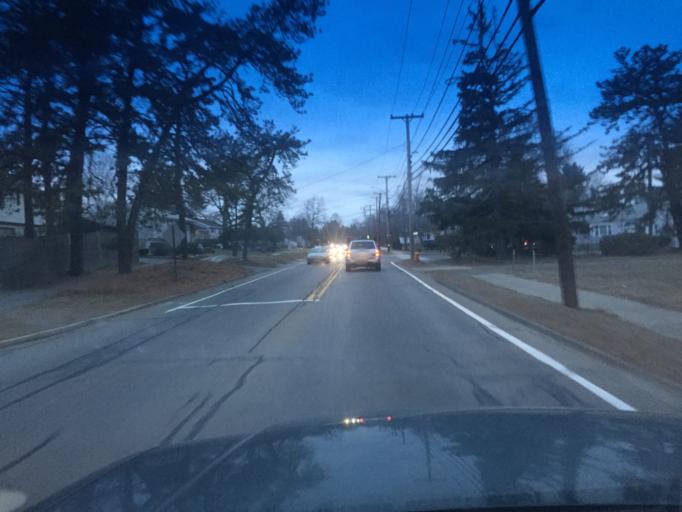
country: US
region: Massachusetts
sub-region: Norfolk County
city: Norwood
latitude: 42.1771
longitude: -71.1786
